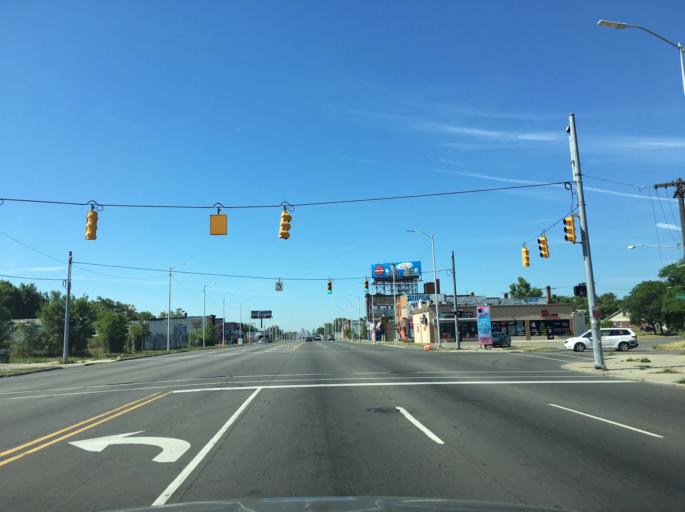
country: US
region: Michigan
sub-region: Macomb County
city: Eastpointe
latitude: 42.4174
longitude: -82.9894
